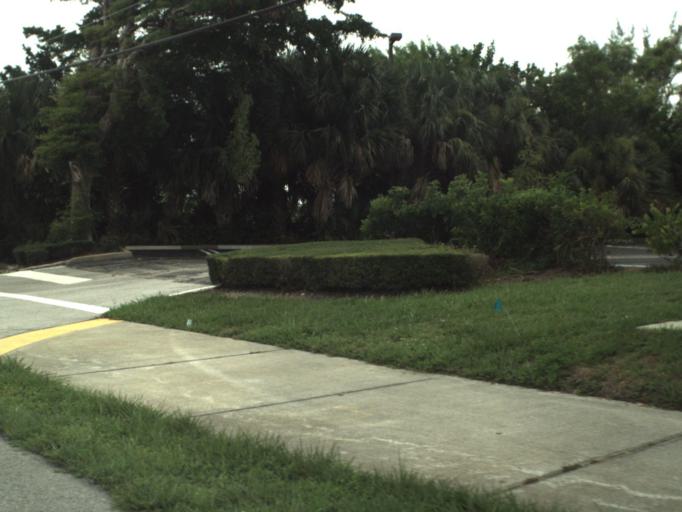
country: US
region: Florida
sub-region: Palm Beach County
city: Jupiter
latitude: 26.9224
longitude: -80.0750
